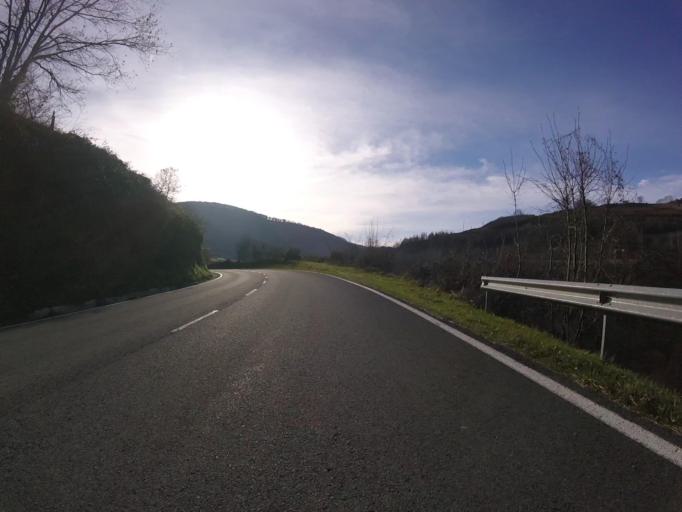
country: ES
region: Navarre
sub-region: Provincia de Navarra
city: Areso
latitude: 43.0928
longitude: -1.9408
